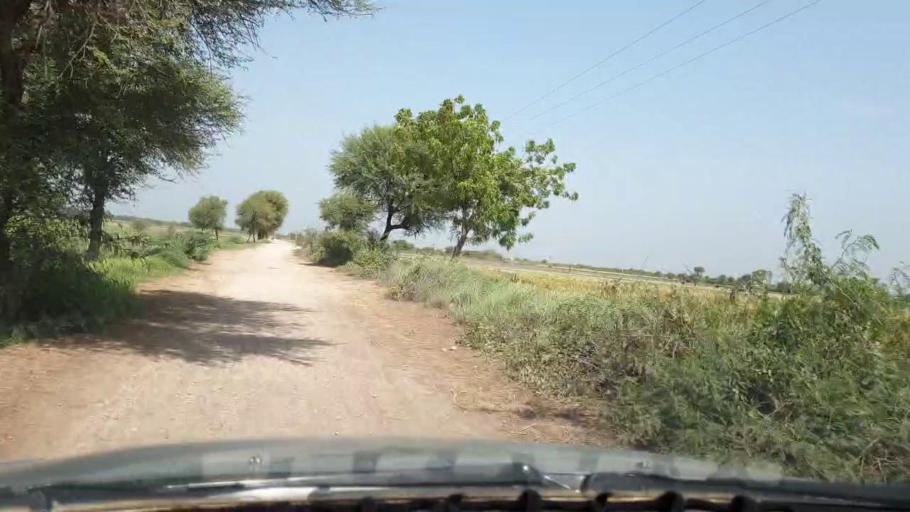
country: PK
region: Sindh
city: Tando Muhammad Khan
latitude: 25.1542
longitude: 68.6337
